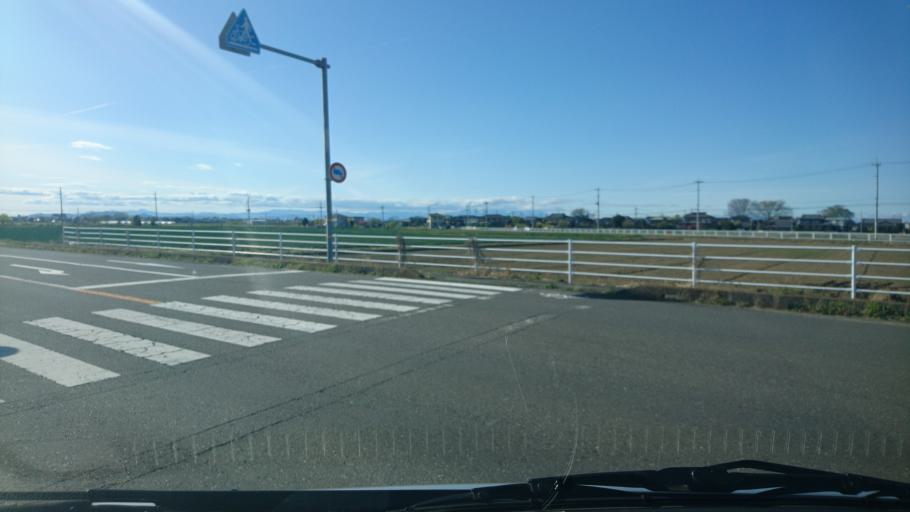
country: JP
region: Ibaraki
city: Yuki
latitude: 36.2813
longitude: 139.8991
